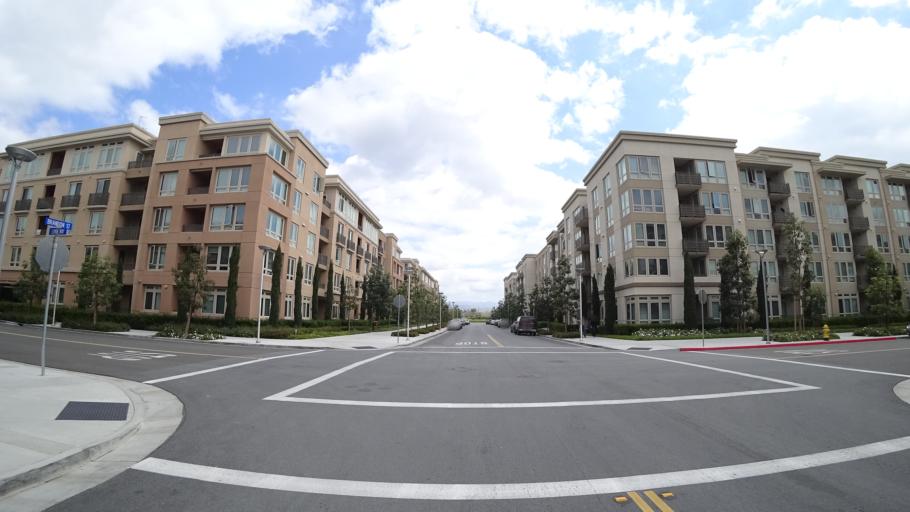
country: US
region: California
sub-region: Santa Clara County
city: Milpitas
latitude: 37.4031
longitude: -121.9428
